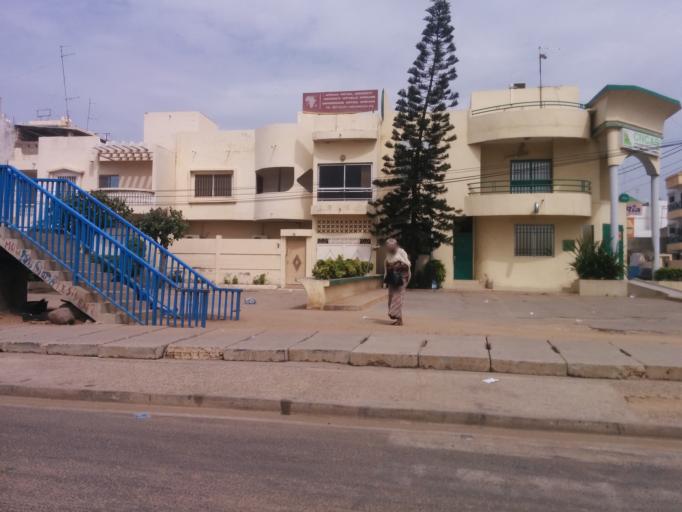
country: SN
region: Dakar
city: Mermoz Boabab
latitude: 14.7271
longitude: -17.4716
